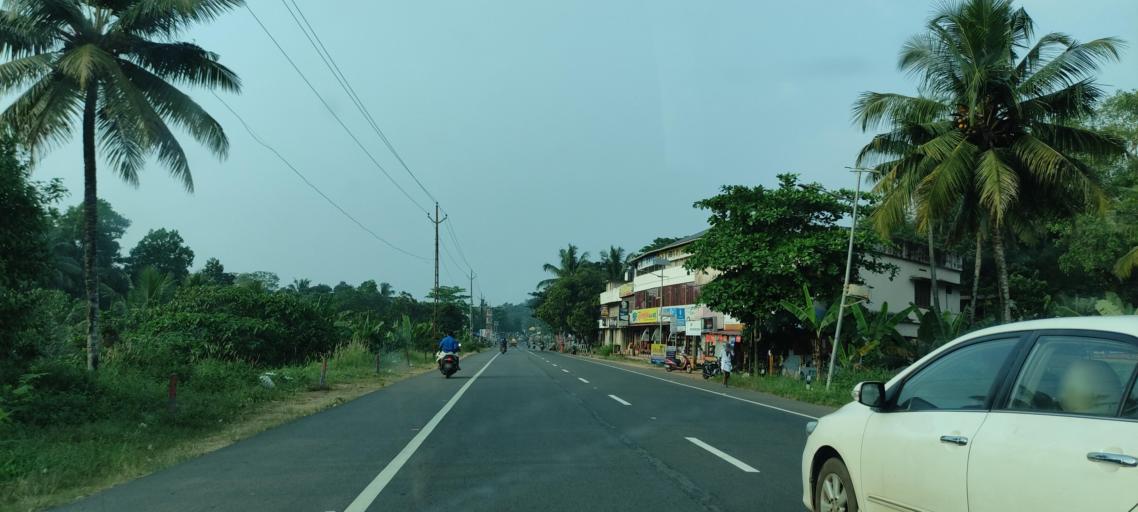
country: IN
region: Kerala
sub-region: Pattanamtitta
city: Adur
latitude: 9.0943
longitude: 76.7529
